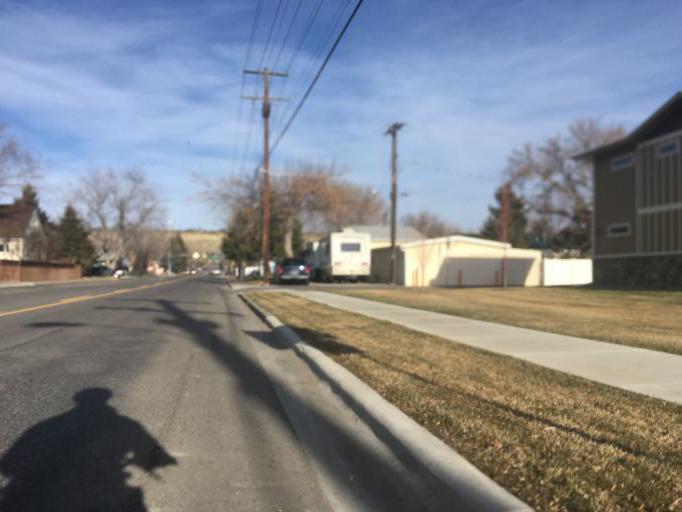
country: US
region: Montana
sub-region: Yellowstone County
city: Billings
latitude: 45.7882
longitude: -108.5590
